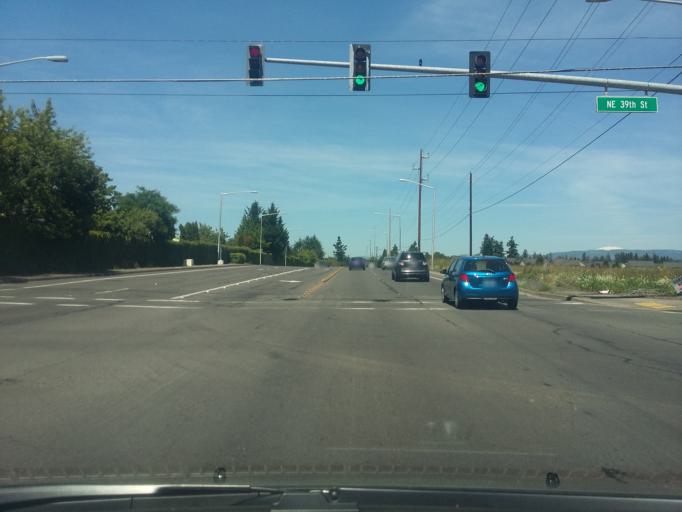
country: US
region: Washington
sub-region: Clark County
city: Mill Plain
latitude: 45.6503
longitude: -122.5060
